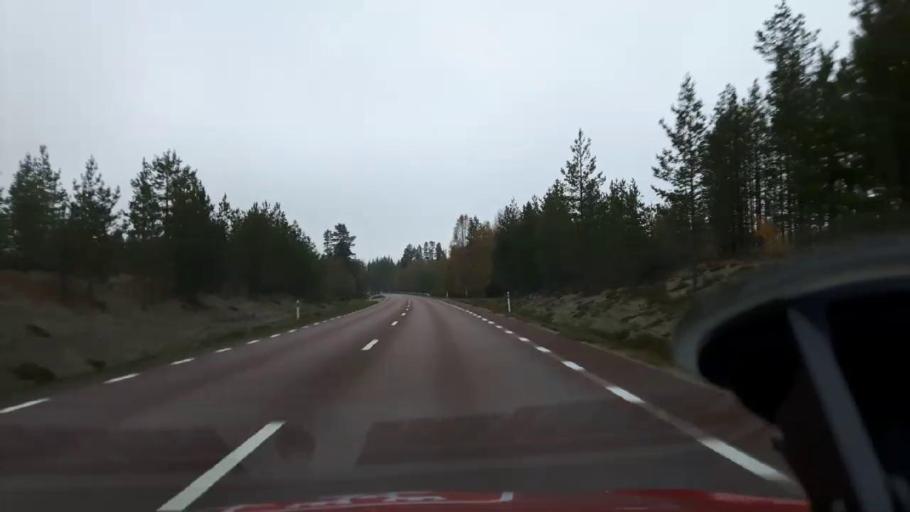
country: SE
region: Jaemtland
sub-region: Bergs Kommun
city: Hoverberg
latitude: 62.5087
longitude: 14.4498
